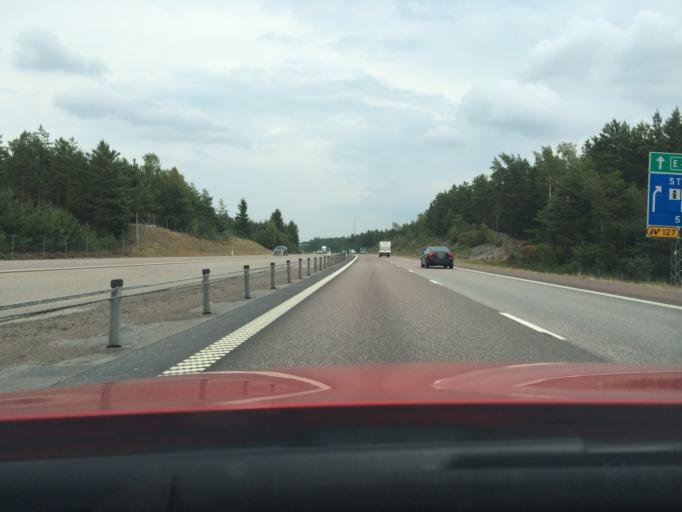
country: SE
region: OEstergoetland
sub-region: Norrkopings Kommun
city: Krokek
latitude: 58.7238
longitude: 16.3934
